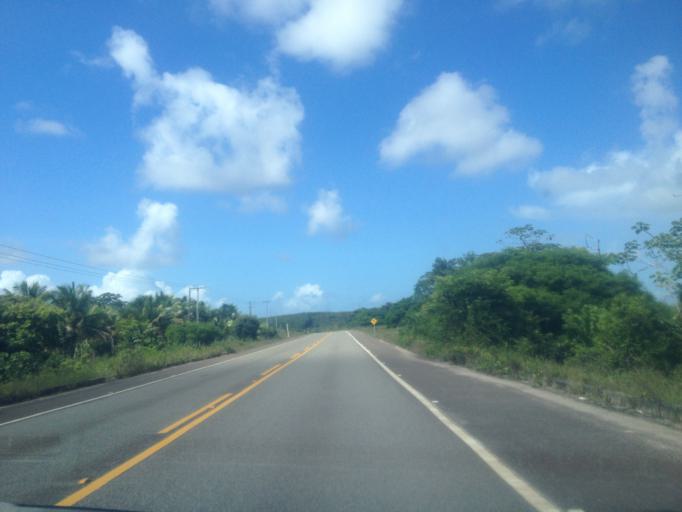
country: BR
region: Sergipe
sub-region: Indiaroba
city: Indiaroba
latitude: -11.4870
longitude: -37.4787
